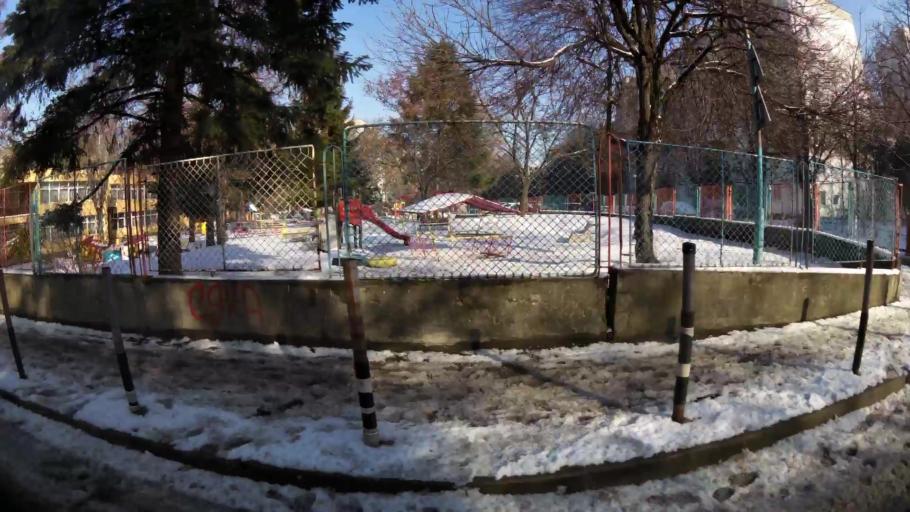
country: BG
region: Sofia-Capital
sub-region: Stolichna Obshtina
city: Sofia
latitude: 42.6627
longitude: 23.3507
